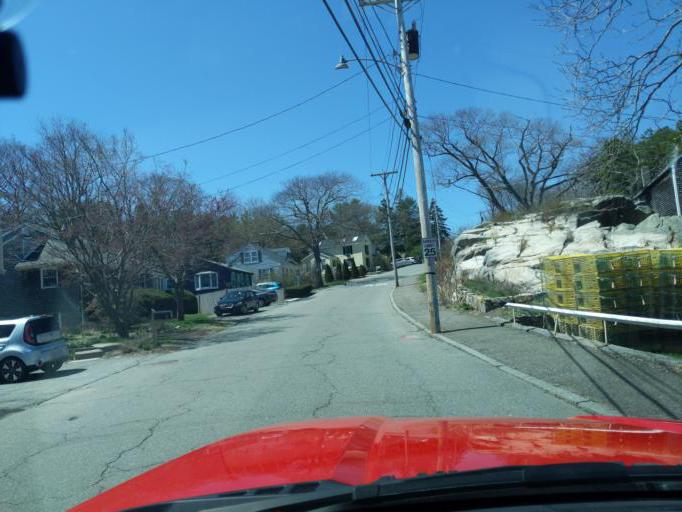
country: US
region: Massachusetts
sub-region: Essex County
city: Rockport
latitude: 42.6759
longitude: -70.6247
